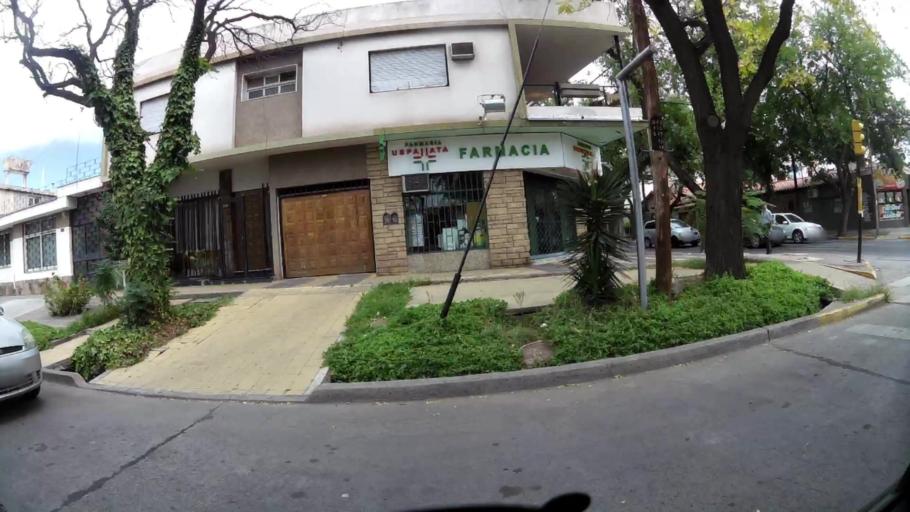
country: AR
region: Mendoza
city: Las Heras
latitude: -32.8692
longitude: -68.8547
